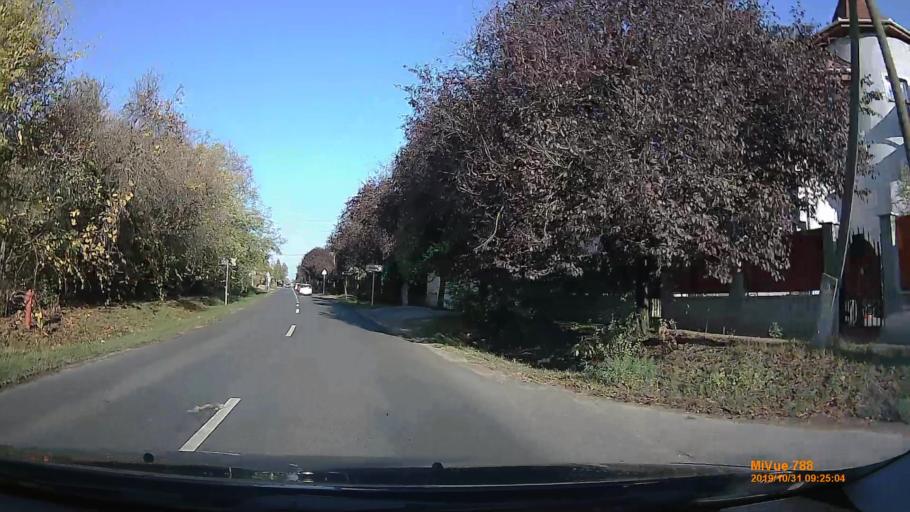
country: HU
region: Pest
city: Maglod
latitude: 47.4398
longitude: 19.3740
